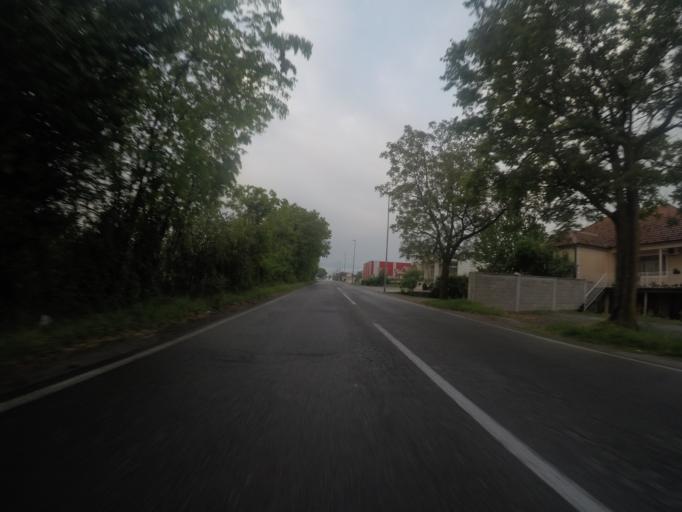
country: ME
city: Mojanovici
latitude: 42.3363
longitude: 19.2211
